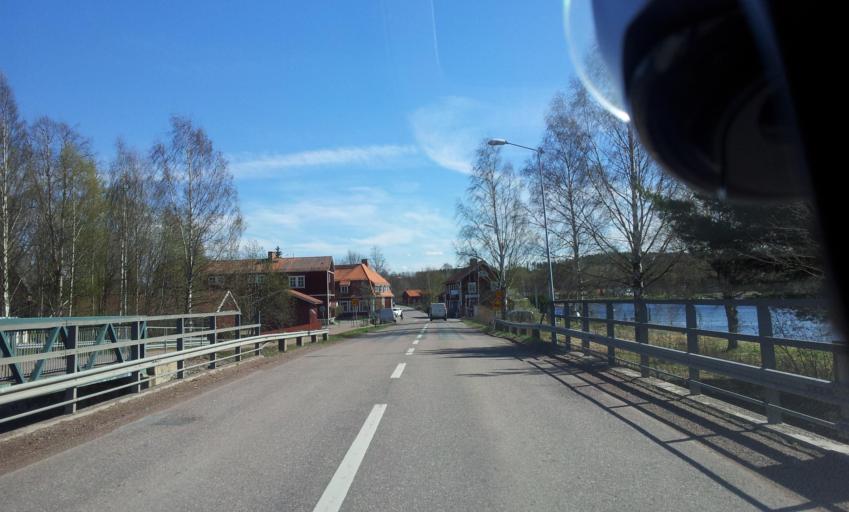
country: SE
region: Dalarna
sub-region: Borlange Kommun
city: Ornas
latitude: 60.4633
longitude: 15.5658
